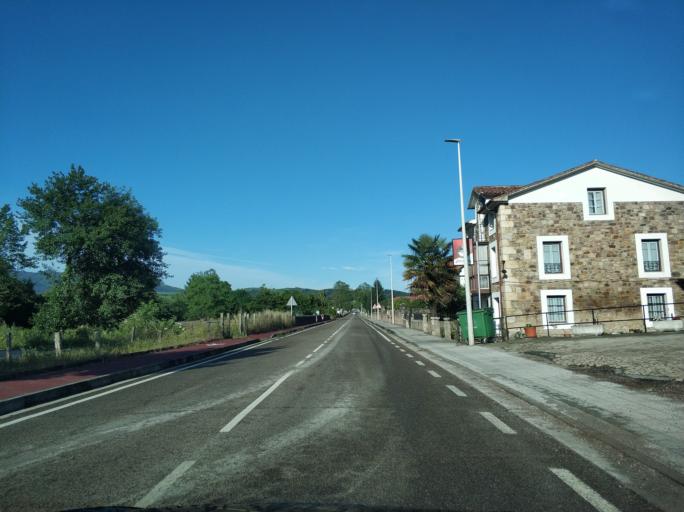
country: ES
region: Cantabria
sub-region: Provincia de Cantabria
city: Polanco
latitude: 43.3535
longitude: -3.9752
